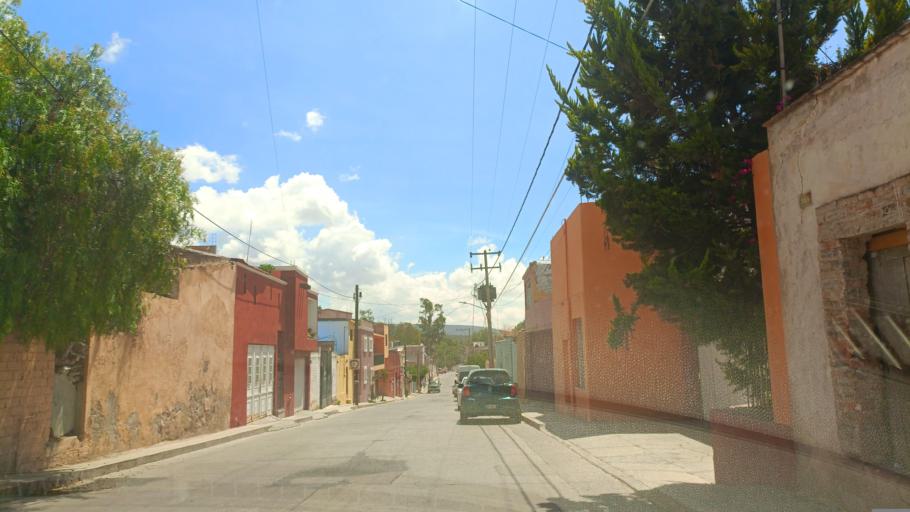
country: MX
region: Guanajuato
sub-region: San Luis de la Paz
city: San Luis de la Paz
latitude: 21.2972
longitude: -100.5111
